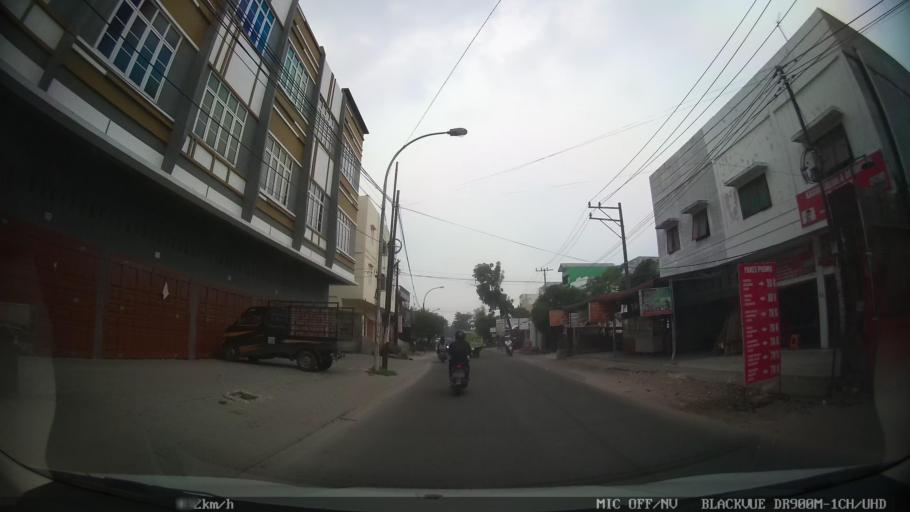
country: ID
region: North Sumatra
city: Medan
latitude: 3.5534
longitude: 98.7031
